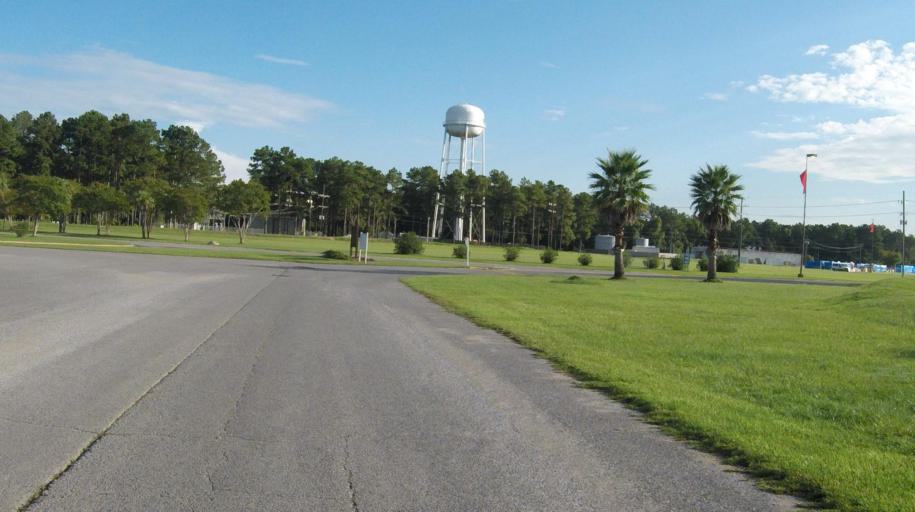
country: US
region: Louisiana
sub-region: Allen Parish
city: Kinder
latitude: 30.5421
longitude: -92.8192
